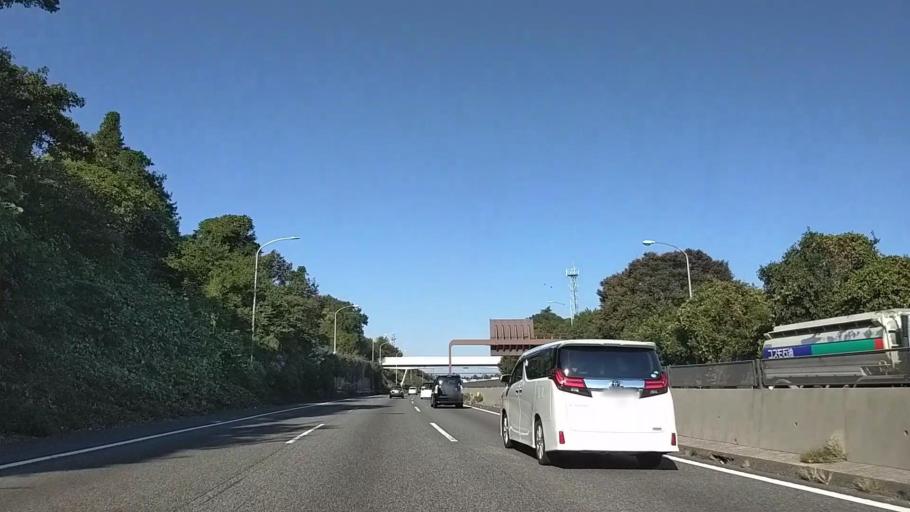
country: JP
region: Kanagawa
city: Yokohama
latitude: 35.4555
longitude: 139.5506
